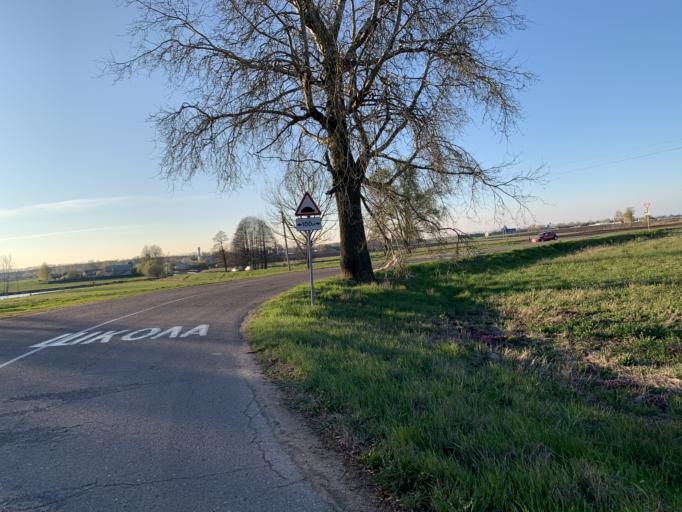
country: BY
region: Minsk
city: Haradzyeya
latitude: 53.3552
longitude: 26.5426
